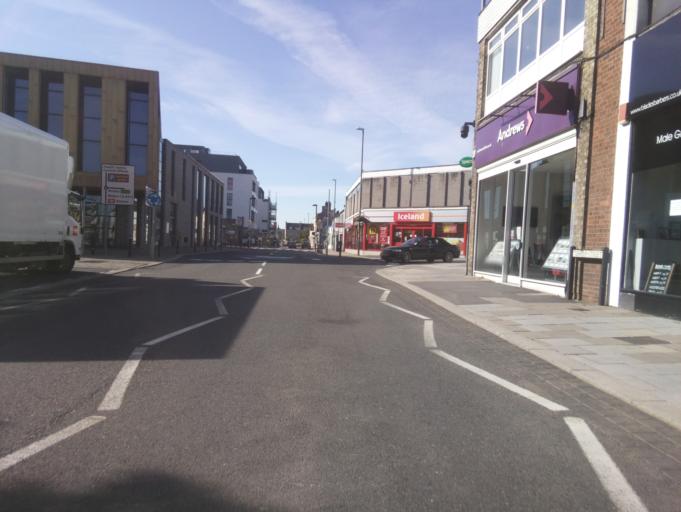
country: GB
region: England
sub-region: Bath and North East Somerset
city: Keynsham
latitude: 51.4143
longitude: -2.4980
